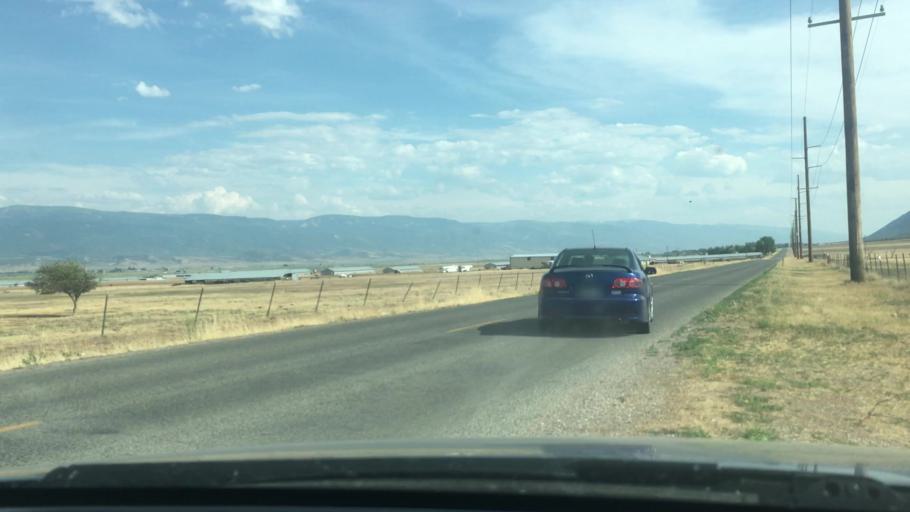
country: US
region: Utah
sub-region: Sanpete County
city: Moroni
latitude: 39.5338
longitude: -111.6399
